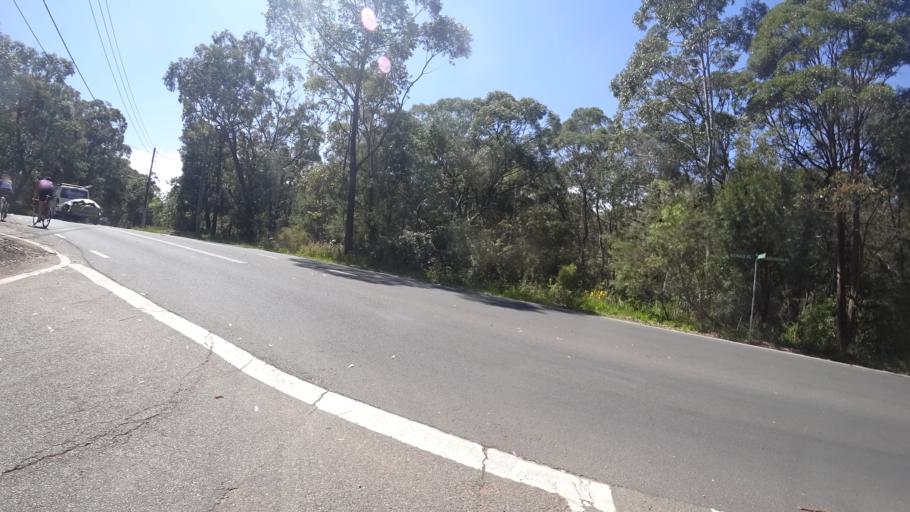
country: AU
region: New South Wales
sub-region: City of Sydney
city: North Turramurra
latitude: -33.6726
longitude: 151.1892
